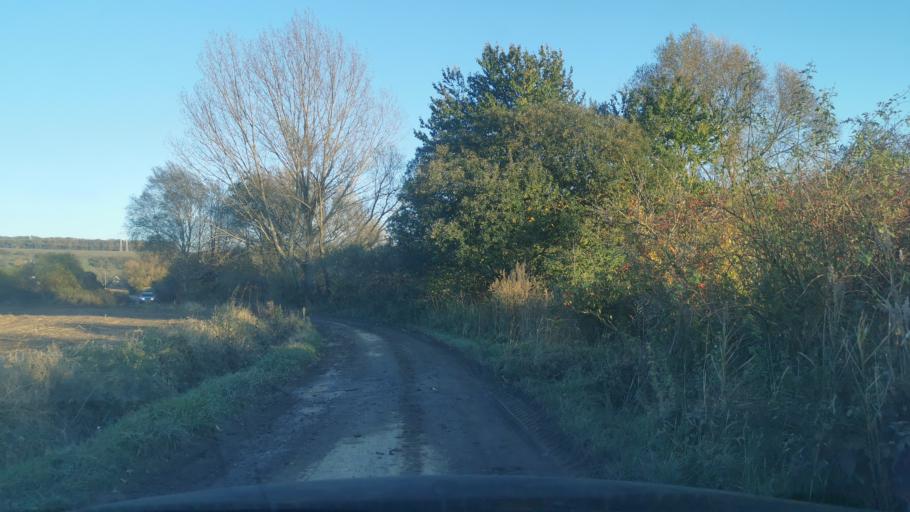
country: SK
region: Trnavsky
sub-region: Okres Senica
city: Senica
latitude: 48.7695
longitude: 17.3265
